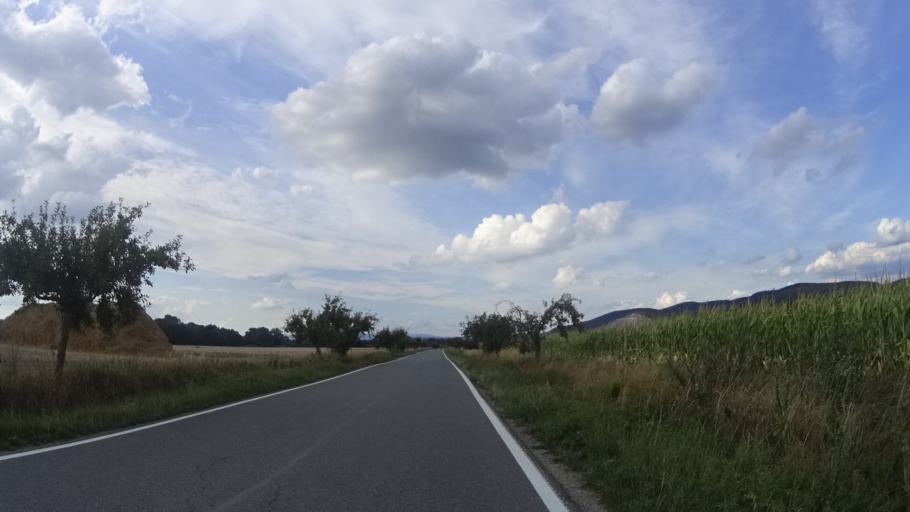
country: CZ
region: Olomoucky
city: Dubicko
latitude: 49.8327
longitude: 16.9361
